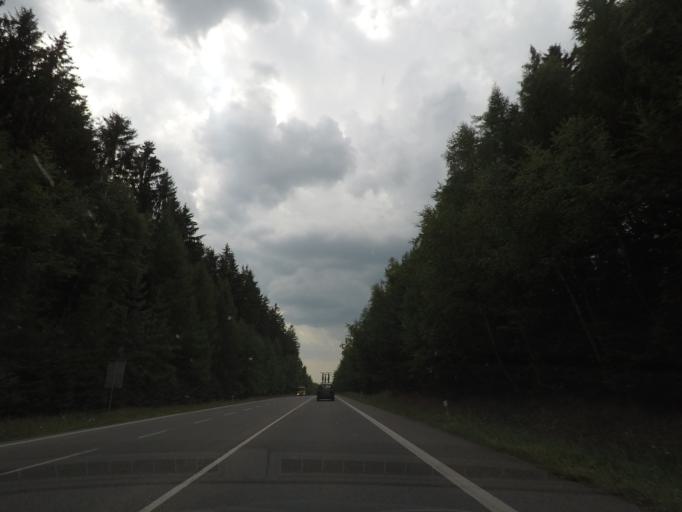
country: CZ
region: Kralovehradecky
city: Nova Paka
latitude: 50.4581
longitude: 15.4852
